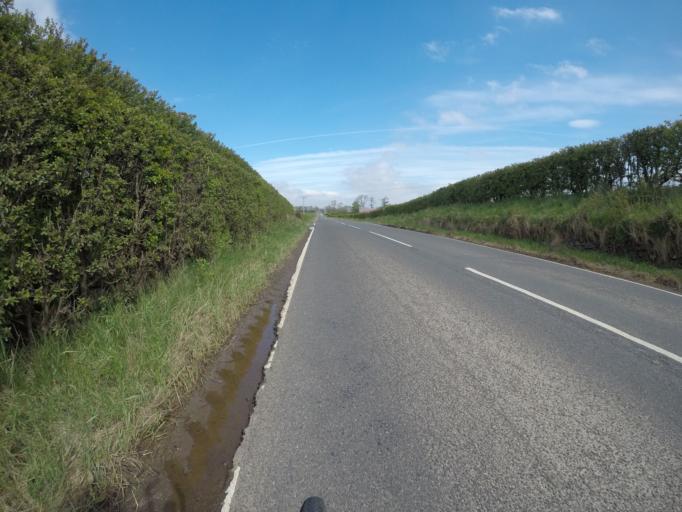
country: GB
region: Scotland
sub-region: East Ayrshire
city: Kilmaurs
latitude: 55.6582
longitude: -4.5540
